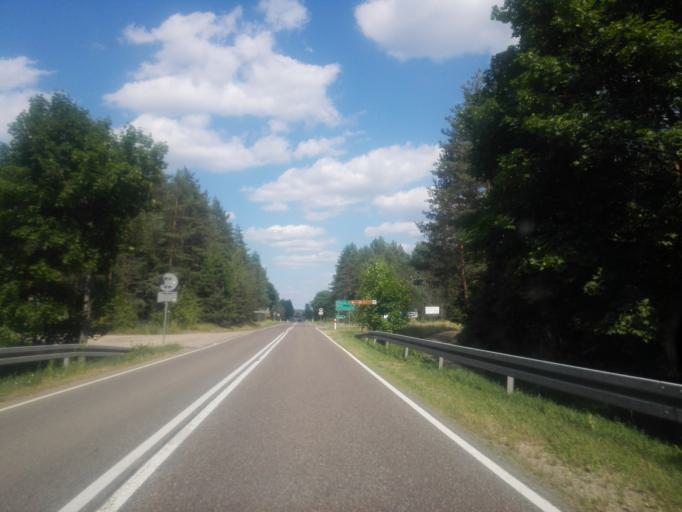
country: PL
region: Podlasie
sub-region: Powiat sejnenski
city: Krasnopol
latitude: 53.9379
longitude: 23.1727
